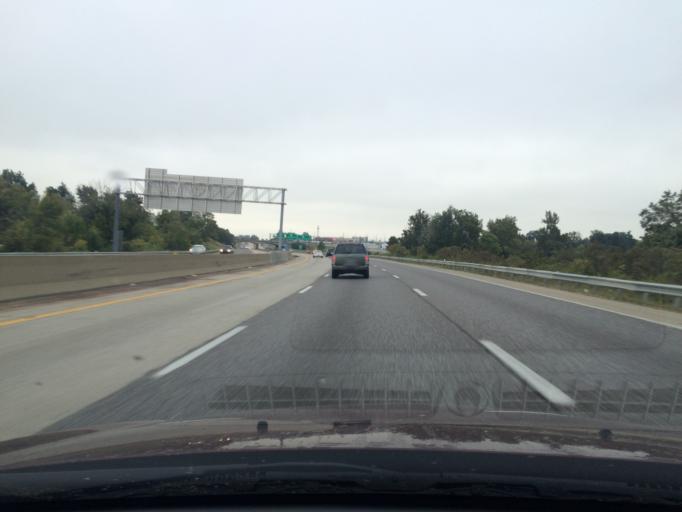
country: US
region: Missouri
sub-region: Saint Louis County
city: Bridgeton
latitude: 38.7436
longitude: -90.4193
